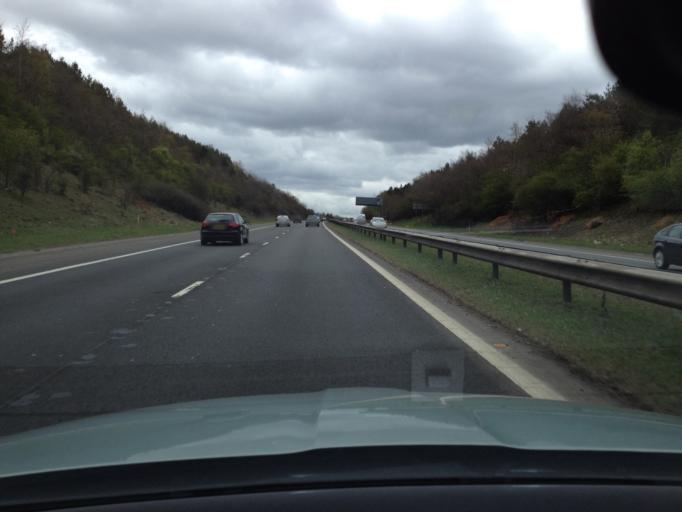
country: GB
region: Scotland
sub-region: North Lanarkshire
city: Cleland
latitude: 55.8414
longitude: -3.9070
